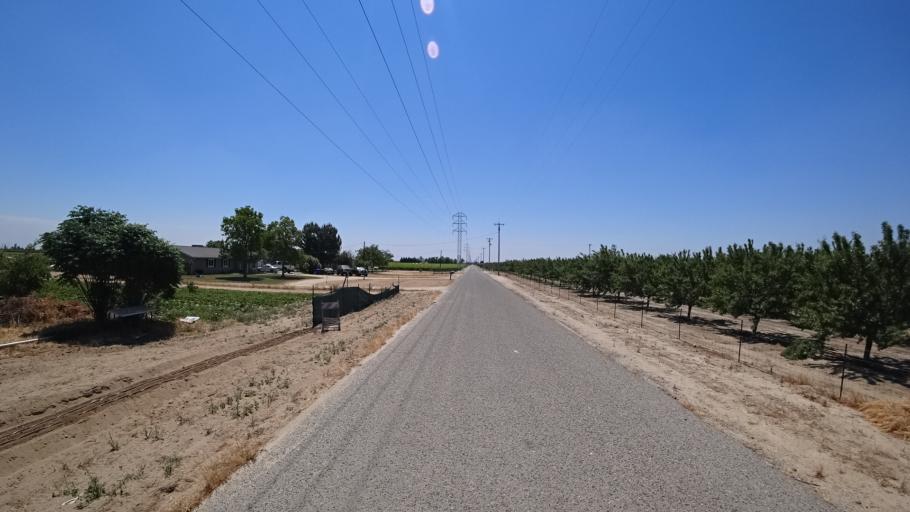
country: US
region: California
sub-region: Fresno County
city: Kingsburg
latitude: 36.4825
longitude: -119.5911
